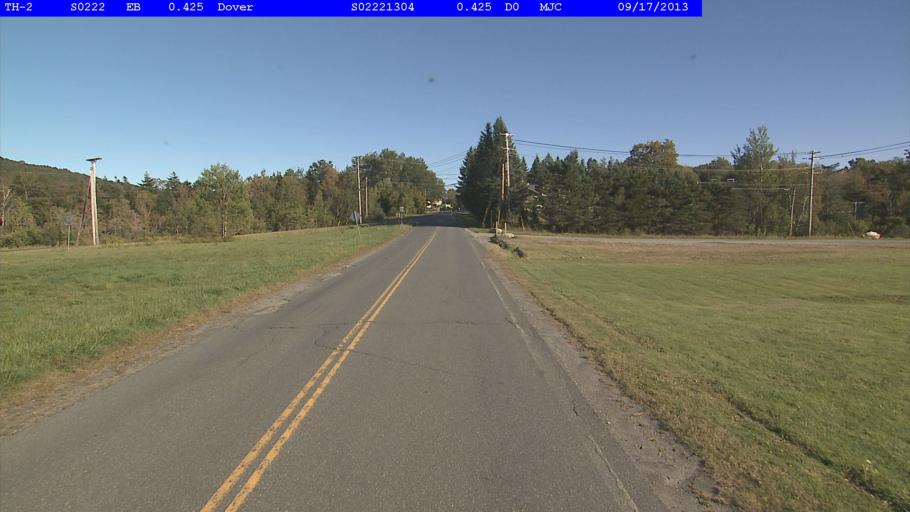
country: US
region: Vermont
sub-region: Windham County
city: Dover
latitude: 42.9538
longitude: -72.8809
